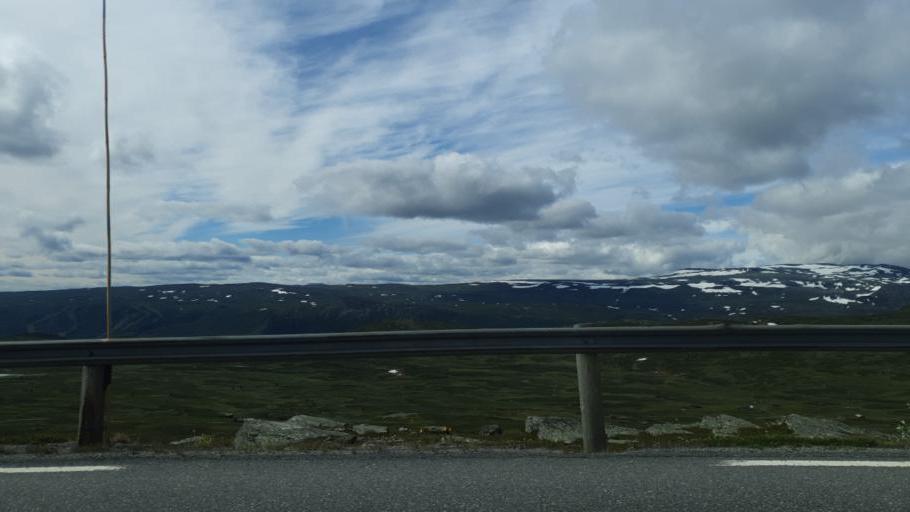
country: NO
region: Oppland
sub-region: Vestre Slidre
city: Slidre
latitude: 61.2861
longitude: 8.8166
